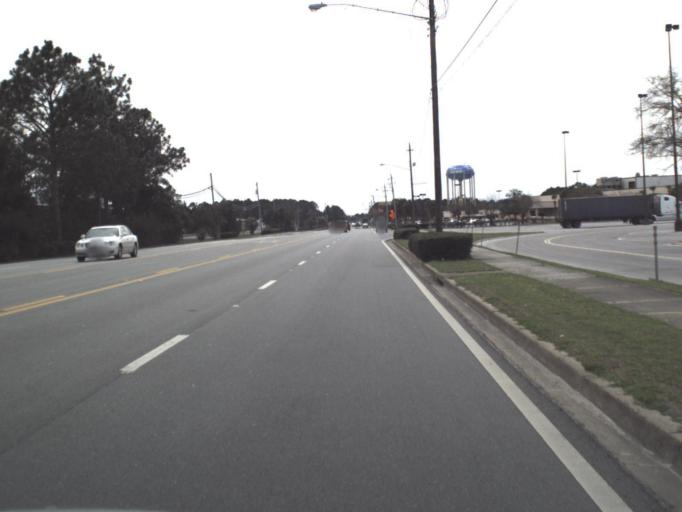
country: US
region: Florida
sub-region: Bay County
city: Hiland Park
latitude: 30.1866
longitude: -85.6451
